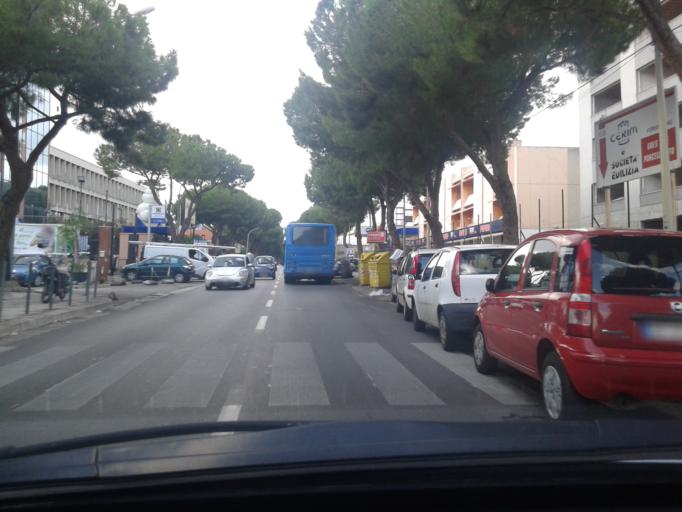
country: IT
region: Sicily
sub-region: Palermo
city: Palermo
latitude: 38.1579
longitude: 13.3176
